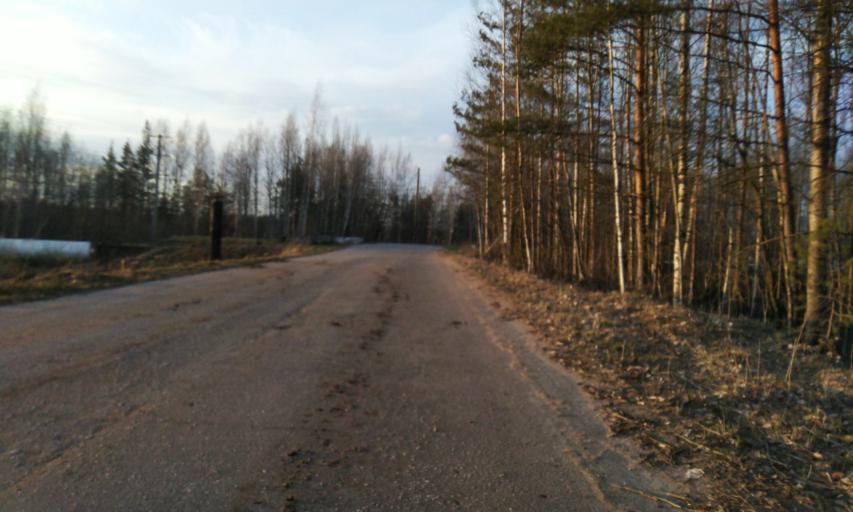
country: RU
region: Leningrad
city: Novoye Devyatkino
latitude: 60.0781
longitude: 30.4675
